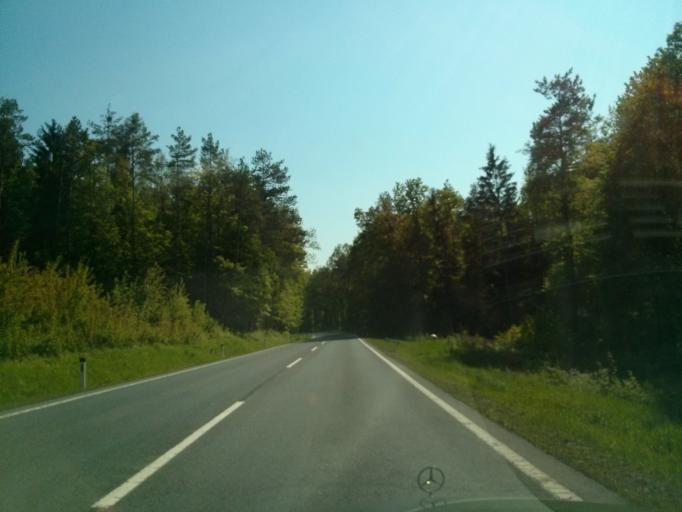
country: AT
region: Burgenland
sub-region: Politischer Bezirk Oberwart
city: Bad Tatzmannsdorf
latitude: 47.3315
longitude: 16.2202
